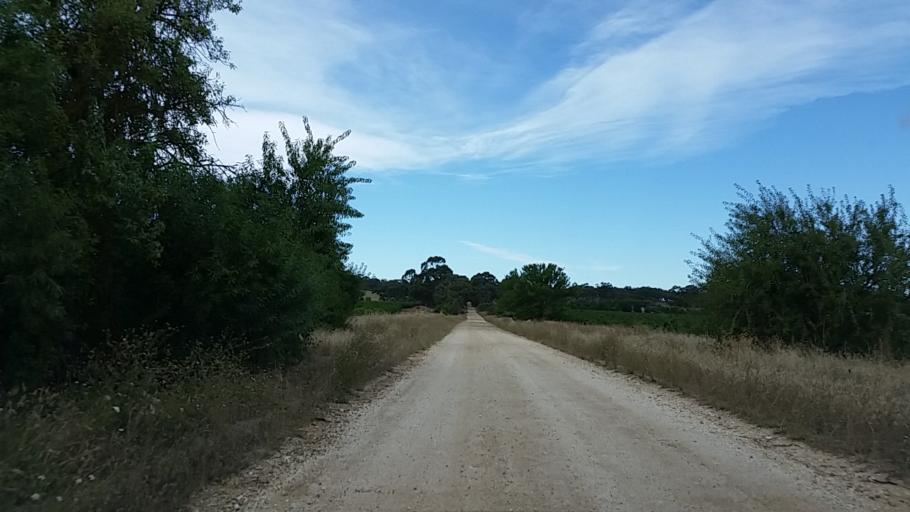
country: AU
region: South Australia
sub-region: Barossa
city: Angaston
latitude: -34.4496
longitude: 139.0473
